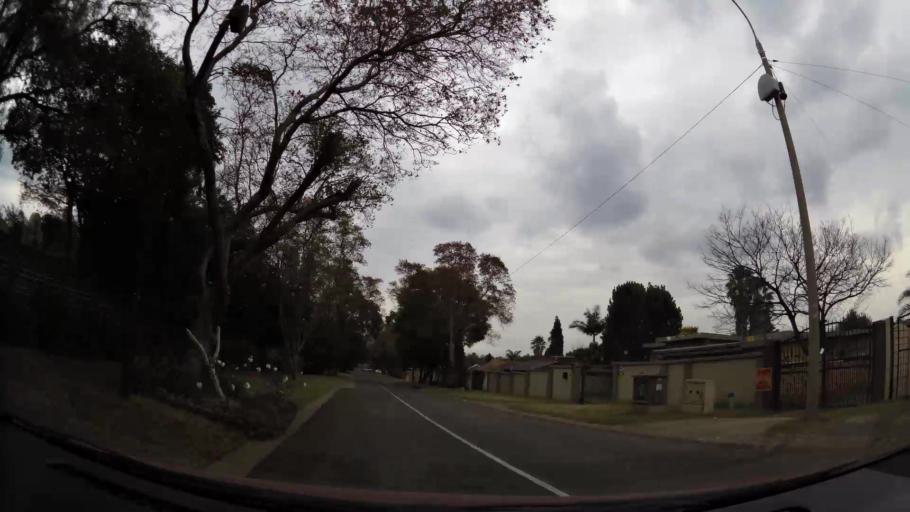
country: ZA
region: Gauteng
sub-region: City of Johannesburg Metropolitan Municipality
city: Roodepoort
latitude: -26.1220
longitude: 27.9063
